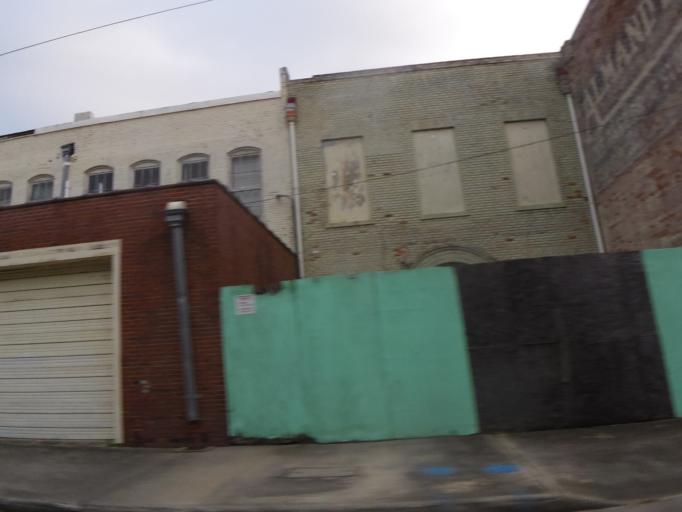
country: US
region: North Carolina
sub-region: Nash County
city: Rocky Mount
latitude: 35.9420
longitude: -77.7961
